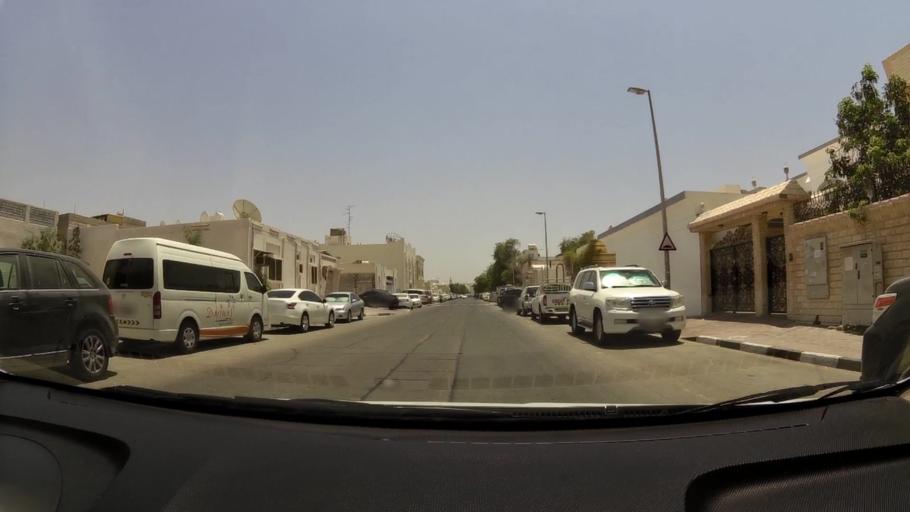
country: AE
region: Ash Shariqah
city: Sharjah
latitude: 25.2905
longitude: 55.3374
